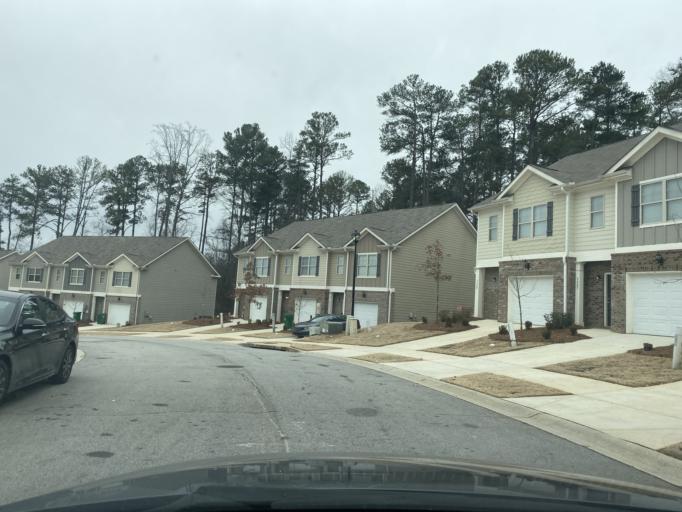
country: US
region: Georgia
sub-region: DeKalb County
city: Pine Mountain
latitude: 33.6911
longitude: -84.1557
